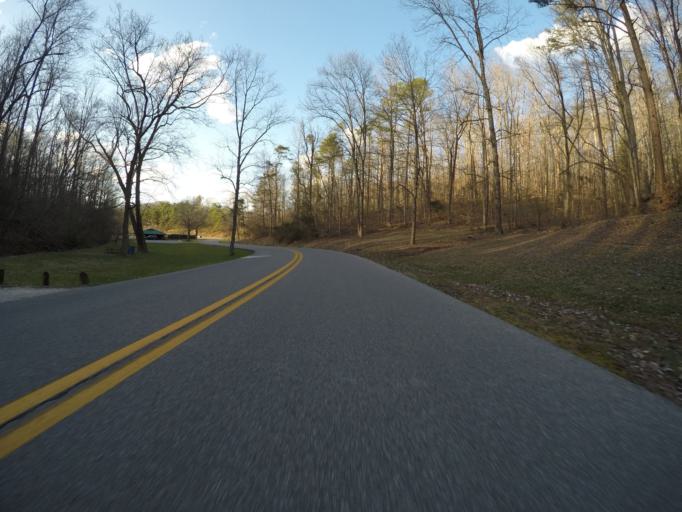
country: US
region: West Virginia
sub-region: Kanawha County
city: Charleston
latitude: 38.3880
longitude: -81.5804
